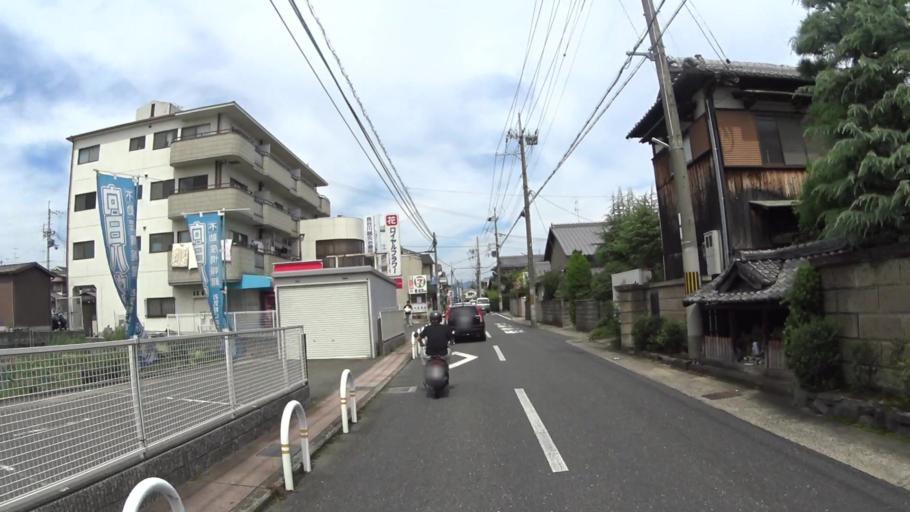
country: JP
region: Kyoto
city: Muko
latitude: 34.9543
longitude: 135.6994
